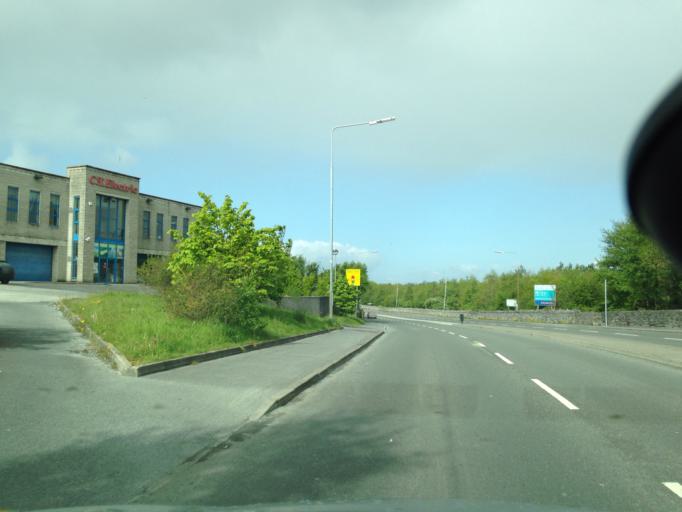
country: IE
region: Connaught
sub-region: County Galway
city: Gaillimh
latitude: 53.2828
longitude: -9.0425
